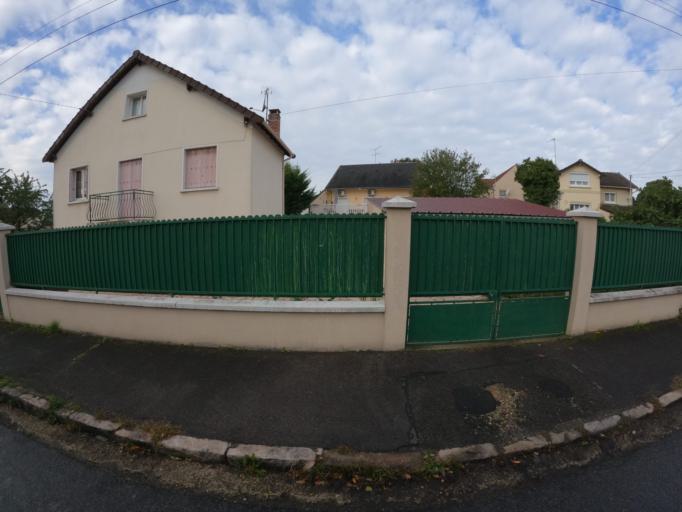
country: FR
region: Ile-de-France
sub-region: Departement de Seine-et-Marne
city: Courtry
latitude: 48.9052
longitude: 2.5978
